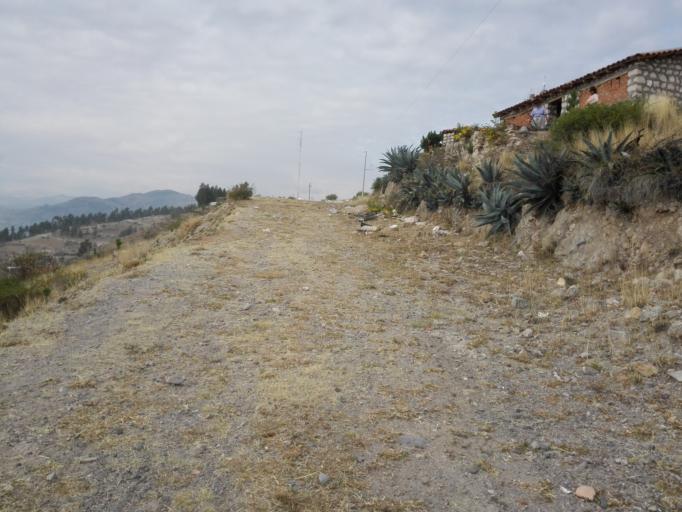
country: PE
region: Ayacucho
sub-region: Provincia de Huamanga
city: Ayacucho
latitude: -13.1436
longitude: -74.2371
